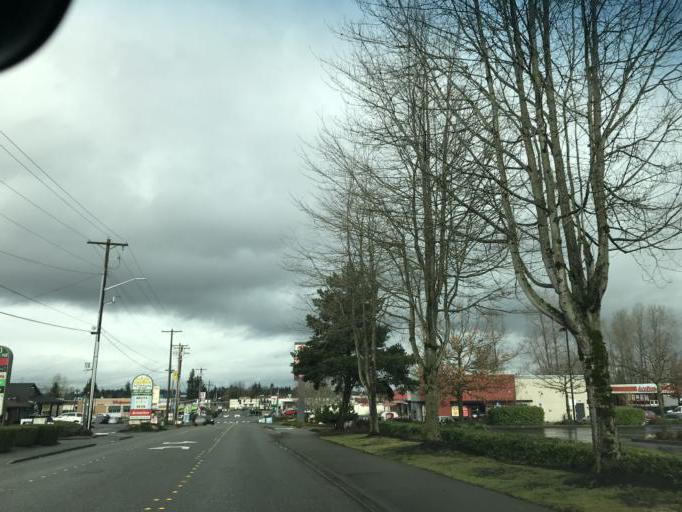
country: US
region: Washington
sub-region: Snohomish County
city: West Lake Stevens
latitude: 48.0004
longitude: -122.1083
